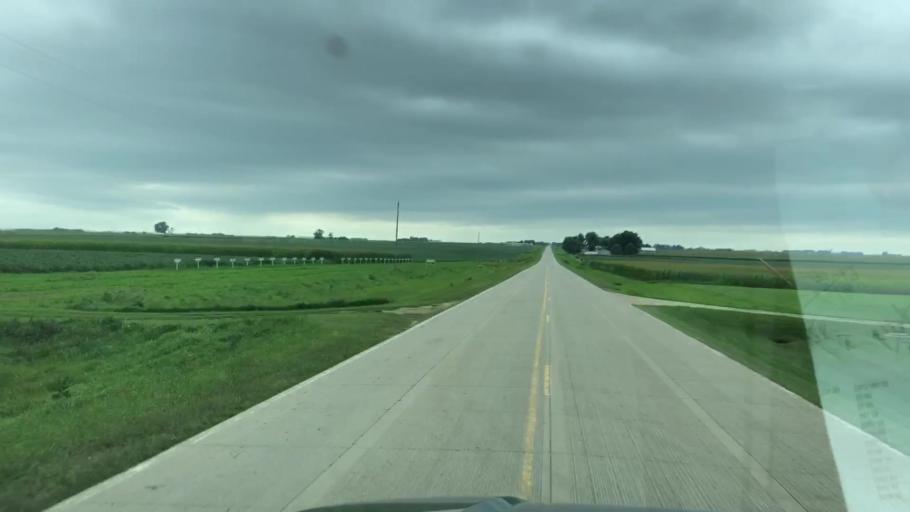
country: US
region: Iowa
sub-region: O'Brien County
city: Sheldon
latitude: 43.1414
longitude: -95.9794
